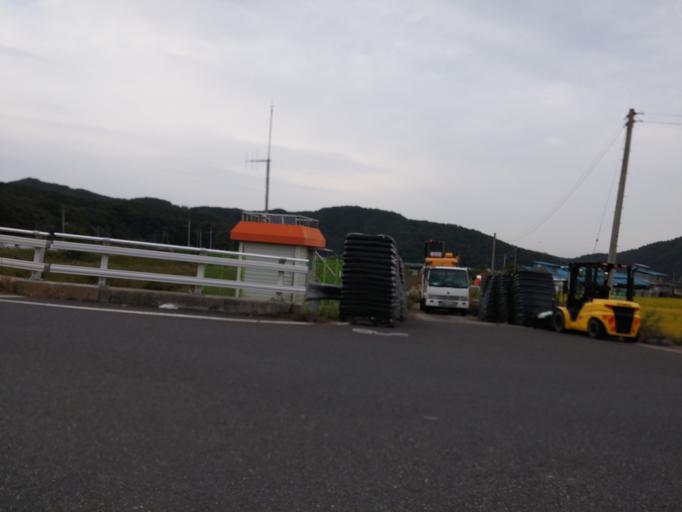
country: KR
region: Daejeon
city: Daejeon
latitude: 36.2473
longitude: 127.3167
